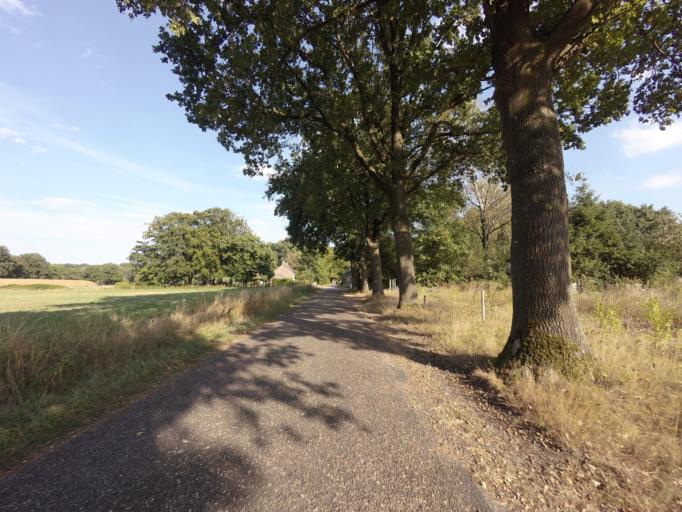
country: NL
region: North Brabant
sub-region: Gemeente Heeze-Leende
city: Heeze
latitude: 51.3592
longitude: 5.5929
